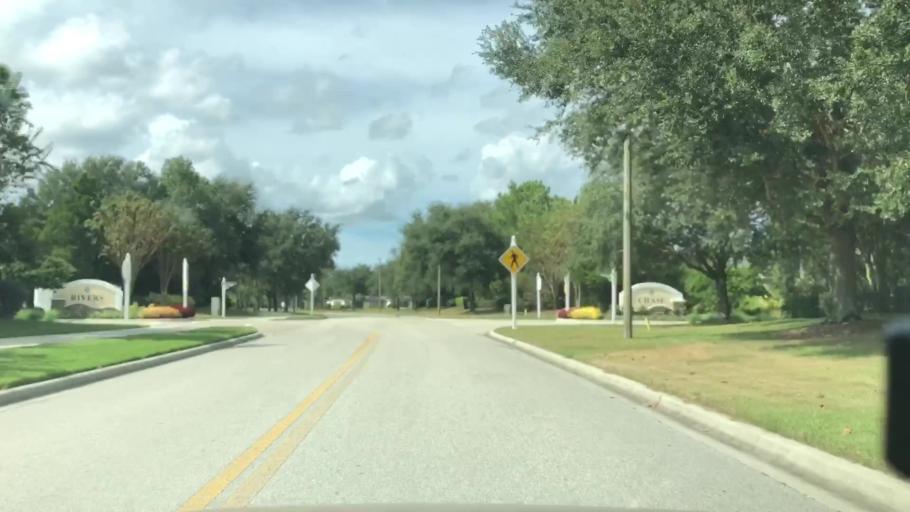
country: US
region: Florida
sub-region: Sarasota County
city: The Meadows
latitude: 27.4257
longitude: -82.4007
